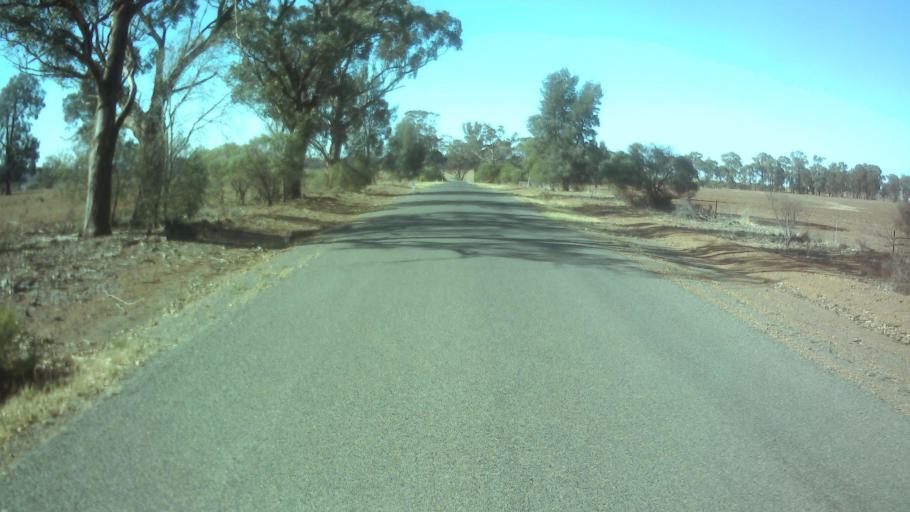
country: AU
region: New South Wales
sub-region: Forbes
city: Forbes
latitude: -33.6972
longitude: 147.8074
